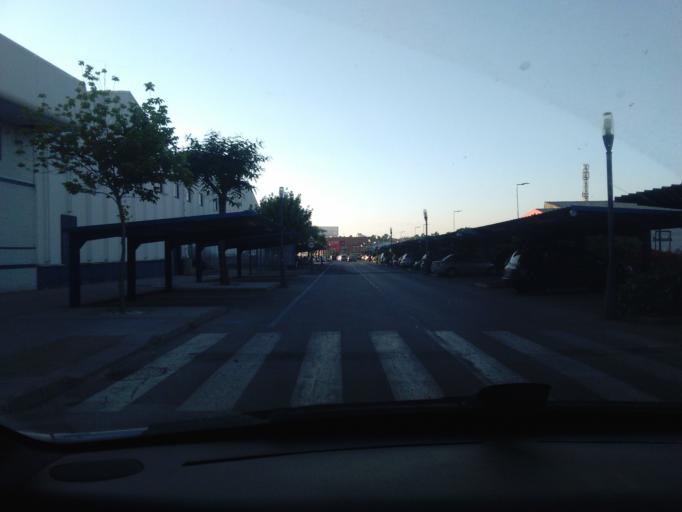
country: ES
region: Andalusia
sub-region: Provincia de Sevilla
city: Sevilla
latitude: 37.3893
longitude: -5.9396
